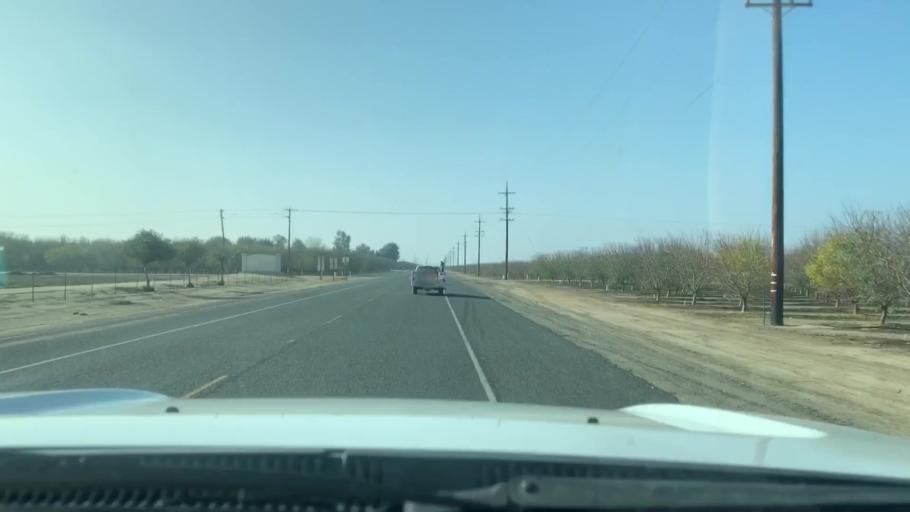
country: US
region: California
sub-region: Kern County
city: Wasco
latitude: 35.6015
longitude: -119.4190
